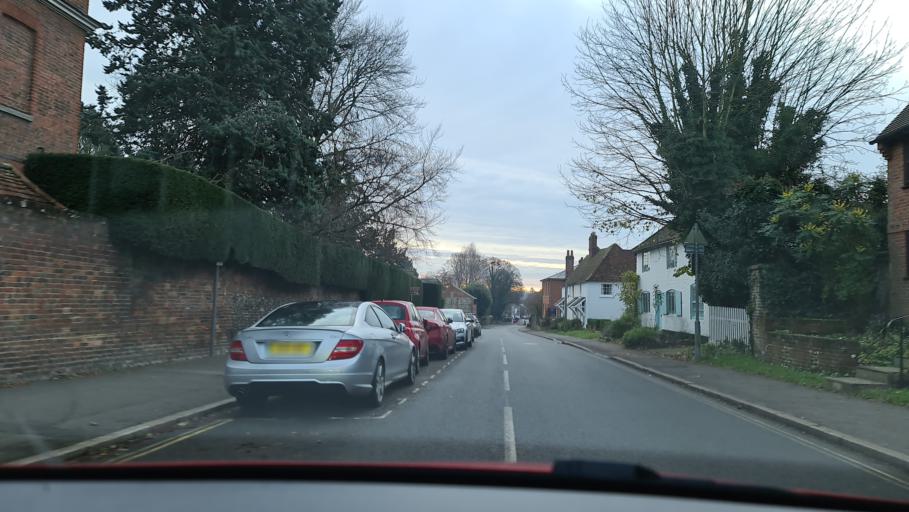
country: GB
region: England
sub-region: Buckinghamshire
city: Great Missenden
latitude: 51.7058
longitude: -0.7094
